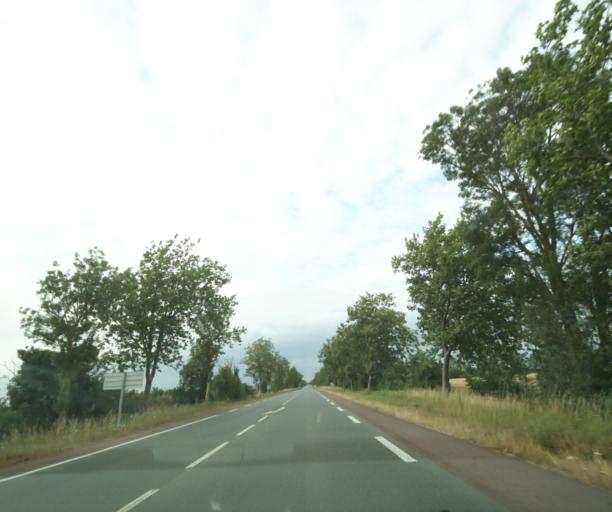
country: FR
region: Poitou-Charentes
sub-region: Departement de la Charente-Maritime
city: Marans
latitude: 46.2866
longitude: -0.9932
